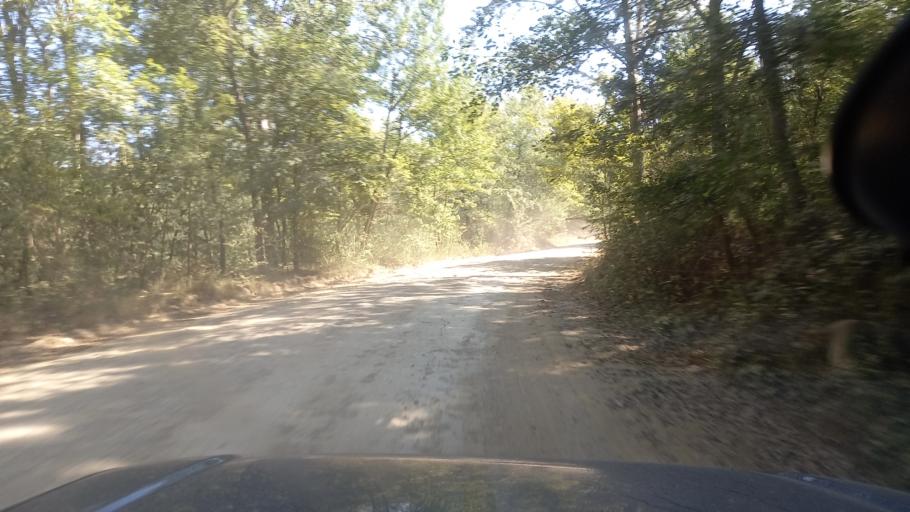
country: RU
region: Krasnodarskiy
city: Azovskaya
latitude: 44.6761
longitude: 38.6371
